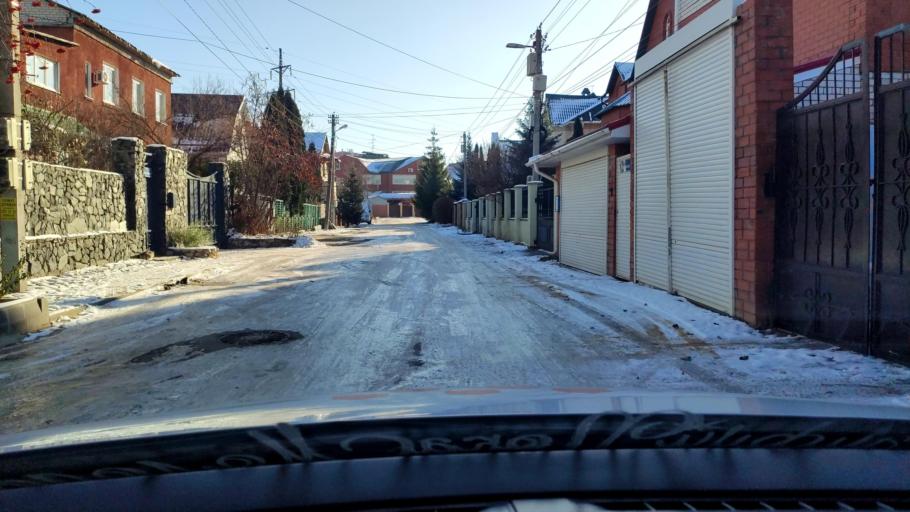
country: RU
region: Voronezj
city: Pridonskoy
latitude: 51.6556
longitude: 39.0976
